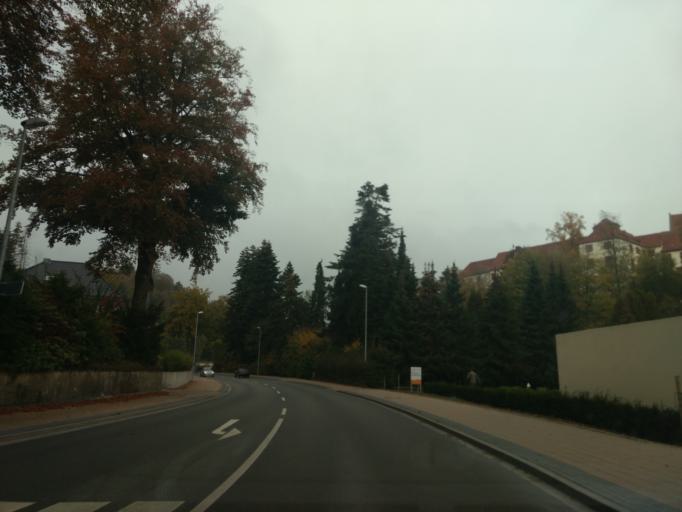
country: DE
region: Lower Saxony
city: Bad Iburg
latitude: 52.1560
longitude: 8.0417
